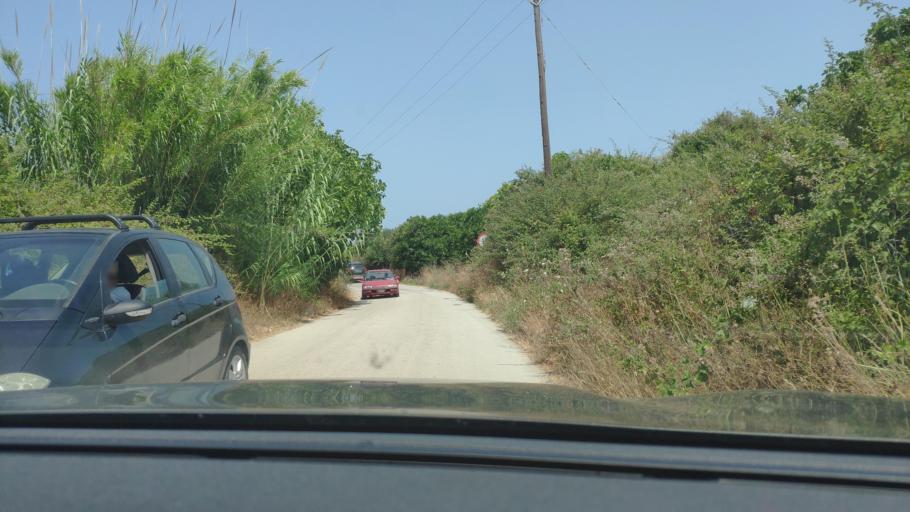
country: GR
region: West Greece
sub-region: Nomos Aitolias kai Akarnanias
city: Menidi
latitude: 39.0528
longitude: 21.0704
